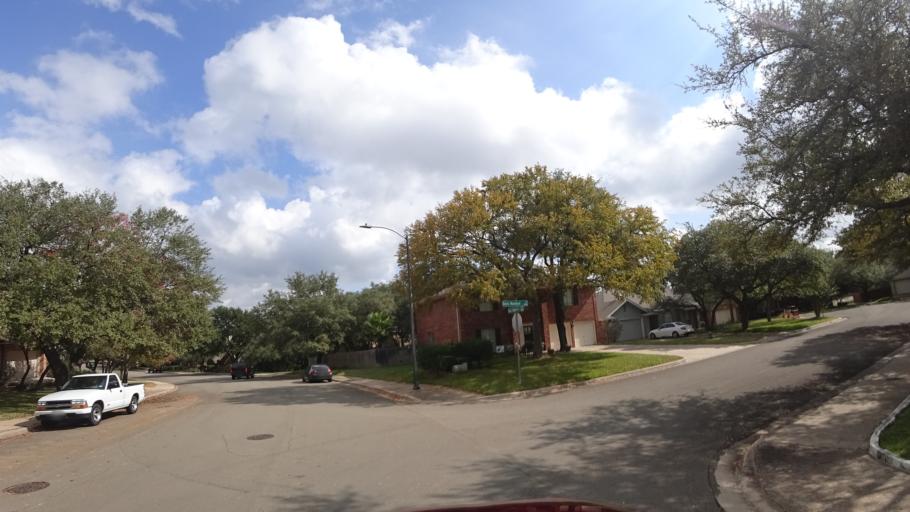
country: US
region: Texas
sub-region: Williamson County
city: Anderson Mill
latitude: 30.4220
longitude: -97.8618
